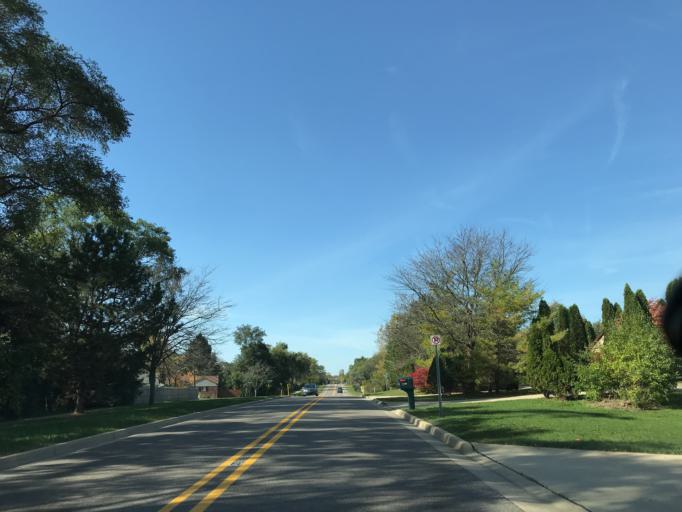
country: US
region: Michigan
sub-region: Oakland County
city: Farmington
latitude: 42.4701
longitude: -83.3603
